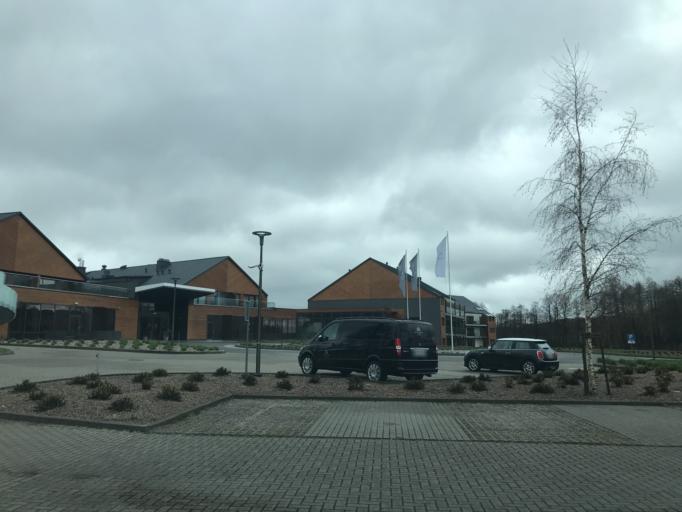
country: PL
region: Warmian-Masurian Voivodeship
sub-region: Powiat olsztynski
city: Stawiguda
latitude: 53.7106
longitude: 20.3768
